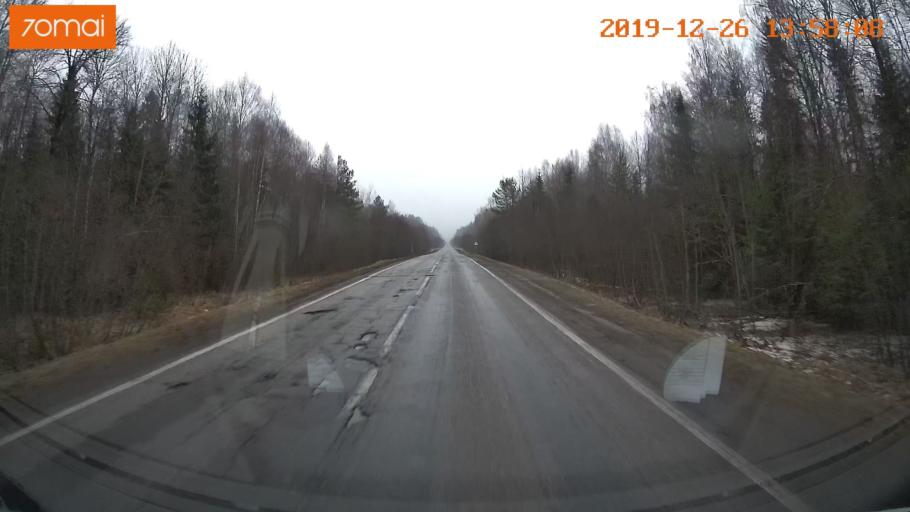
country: RU
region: Jaroslavl
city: Poshekhon'ye
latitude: 58.5766
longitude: 38.6942
